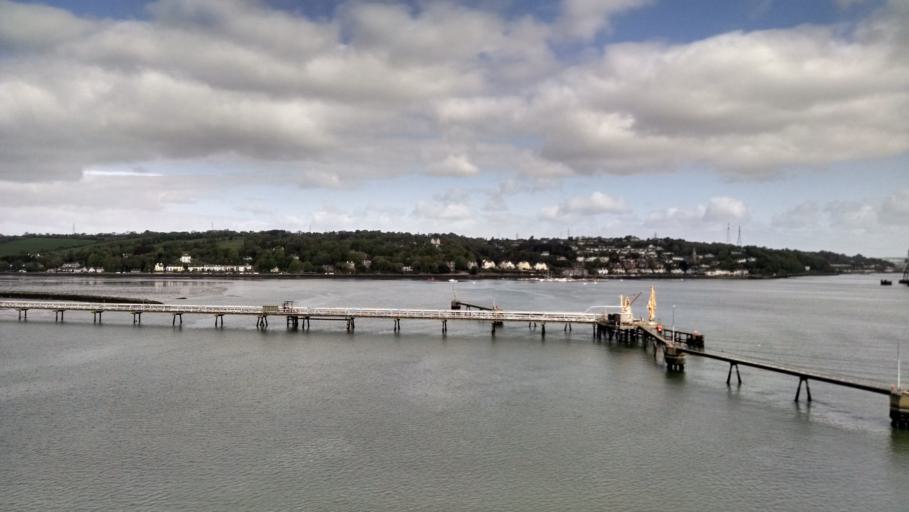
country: IE
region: Munster
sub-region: County Cork
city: Cobh
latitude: 51.8375
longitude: -8.3249
